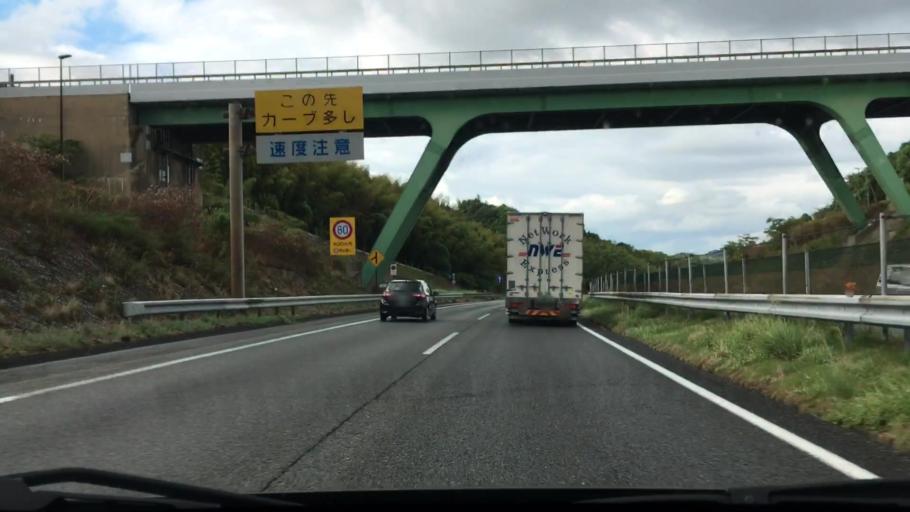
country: JP
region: Fukuoka
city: Nishifukuma
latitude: 33.7396
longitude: 130.5197
